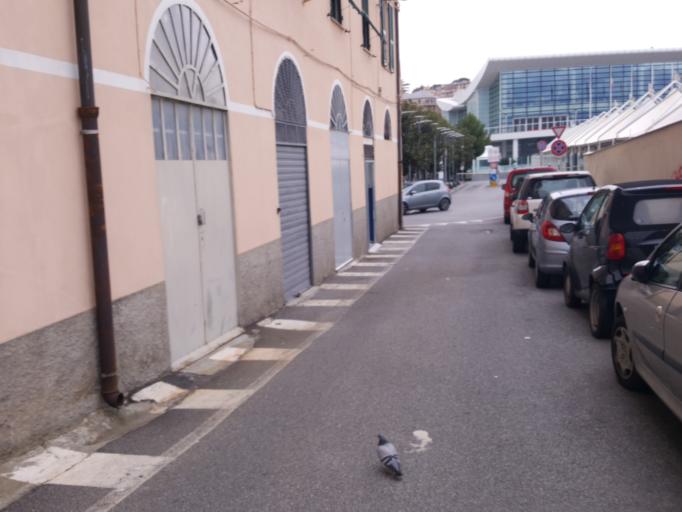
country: IT
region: Liguria
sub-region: Provincia di Savona
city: Savona
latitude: 44.3088
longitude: 8.4880
